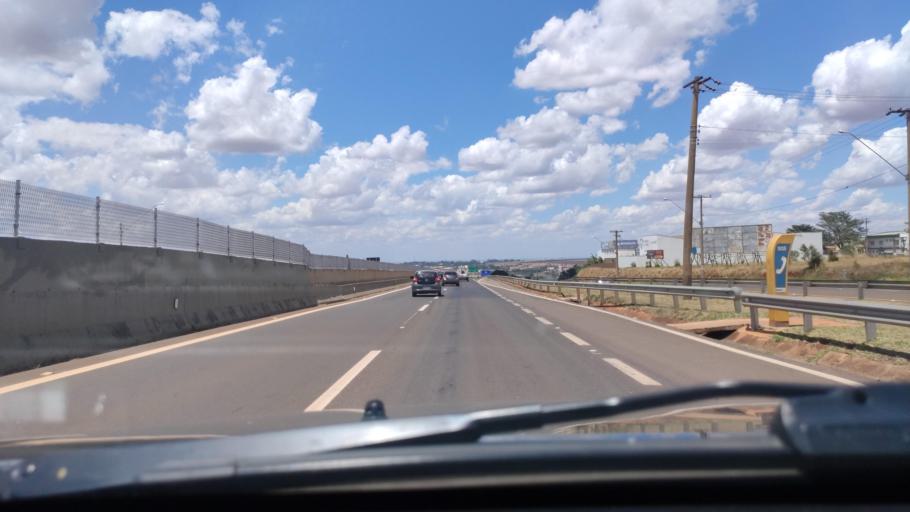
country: BR
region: Sao Paulo
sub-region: Jau
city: Jau
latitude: -22.2614
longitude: -48.5543
